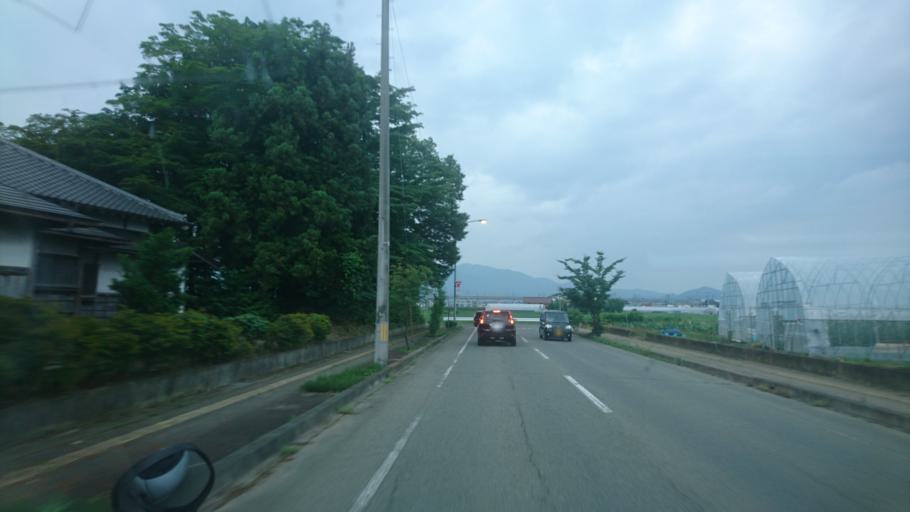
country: JP
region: Iwate
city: Morioka-shi
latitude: 39.6462
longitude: 141.1573
